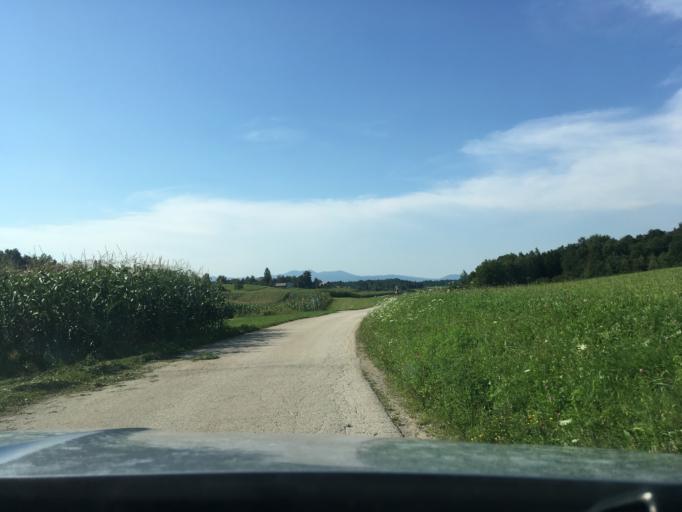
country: SI
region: Crnomelj
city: Crnomelj
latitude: 45.4652
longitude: 15.2113
